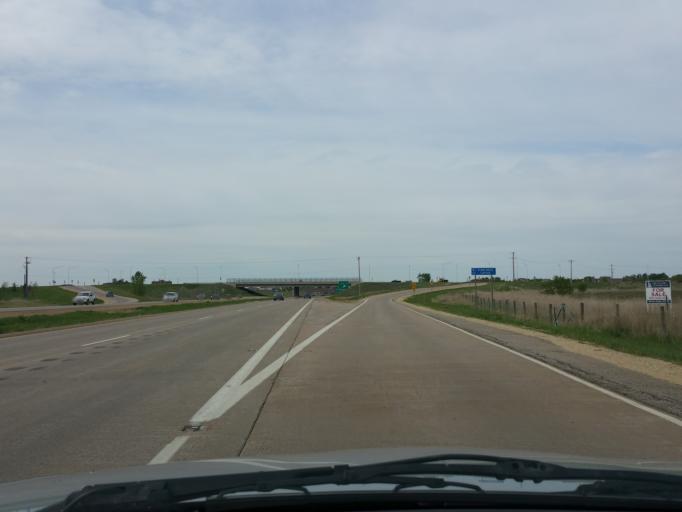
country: US
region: Wisconsin
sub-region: Saint Croix County
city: Hudson
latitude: 44.9451
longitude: -92.6944
